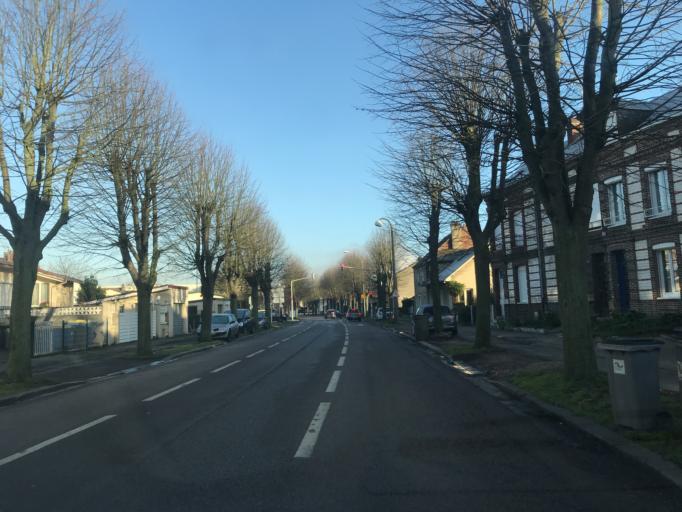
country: FR
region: Haute-Normandie
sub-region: Departement de la Seine-Maritime
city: Sotteville-les-Rouen
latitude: 49.4158
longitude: 1.0983
